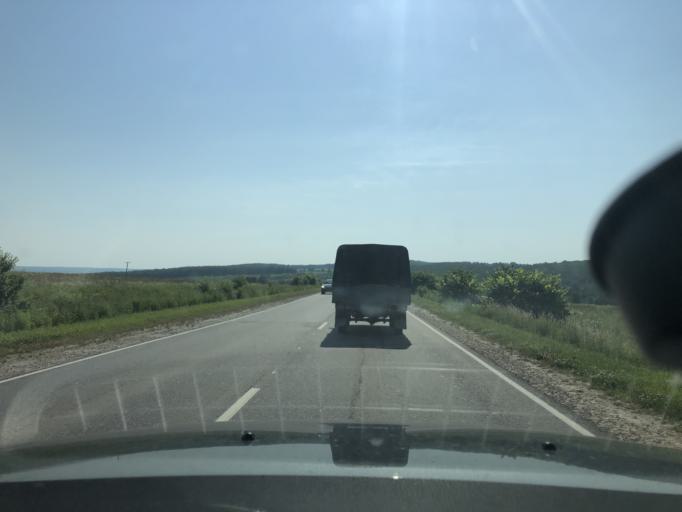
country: RU
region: Tula
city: Dubna
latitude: 54.1319
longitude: 37.0342
